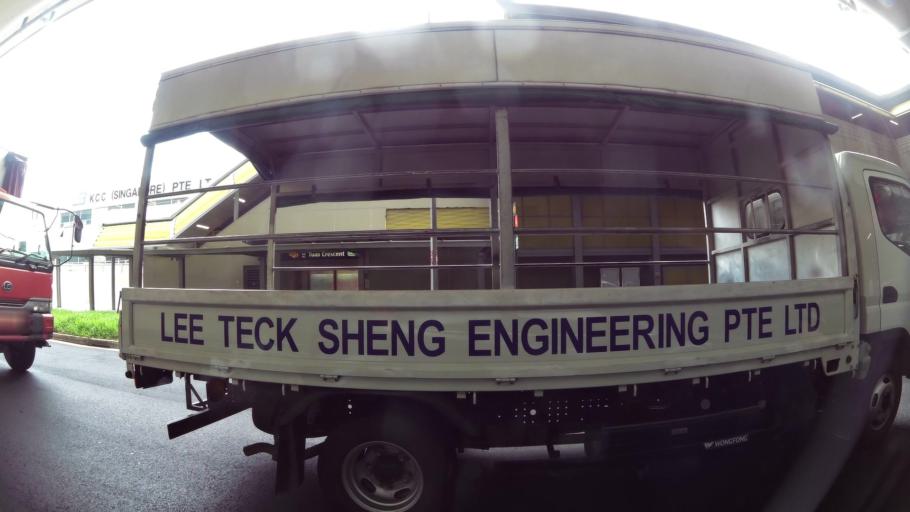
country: MY
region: Johor
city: Johor Bahru
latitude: 1.3210
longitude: 103.6491
